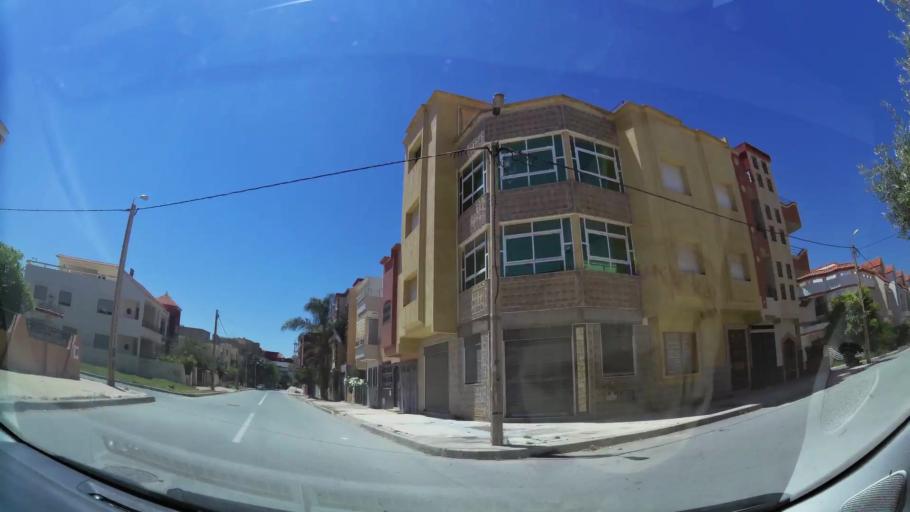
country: MA
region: Oriental
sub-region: Berkane-Taourirt
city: Madagh
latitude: 35.0827
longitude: -2.2271
